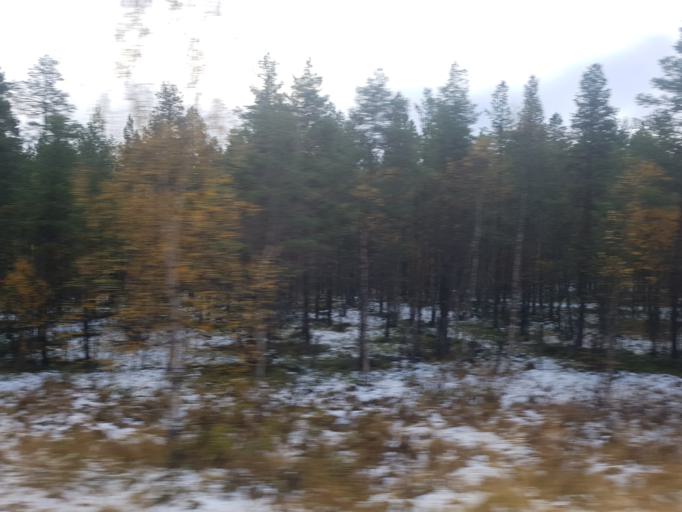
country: NO
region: Sor-Trondelag
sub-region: Oppdal
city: Oppdal
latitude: 62.6372
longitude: 9.8047
